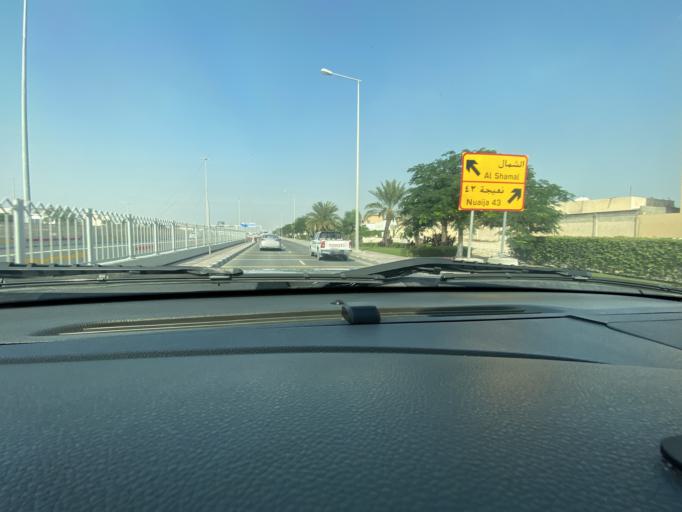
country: QA
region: Baladiyat ad Dawhah
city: Doha
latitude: 25.2464
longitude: 51.5138
